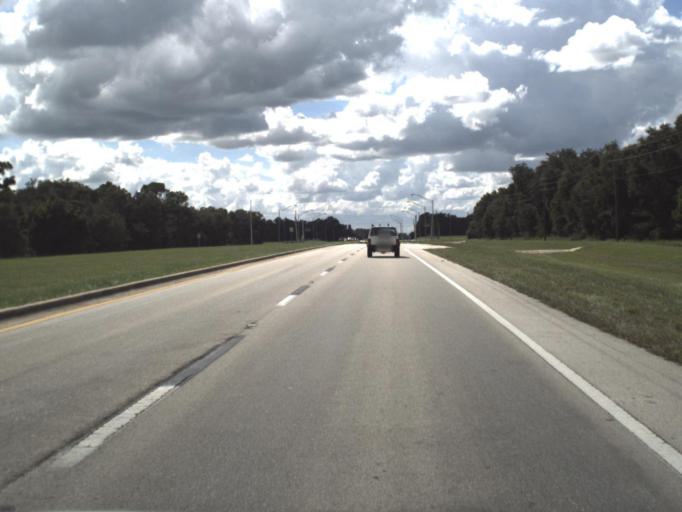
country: US
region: Florida
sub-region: Polk County
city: Jan-Phyl Village
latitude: 28.0107
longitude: -81.8168
